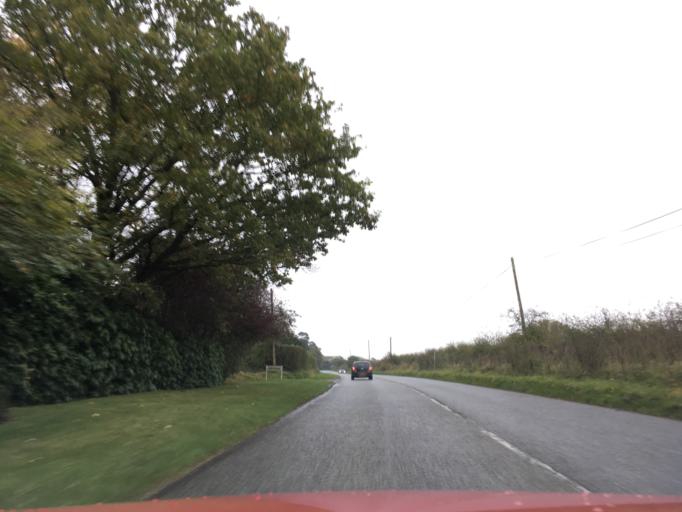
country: GB
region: England
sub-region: West Berkshire
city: Winterbourne
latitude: 51.4125
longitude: -1.3656
